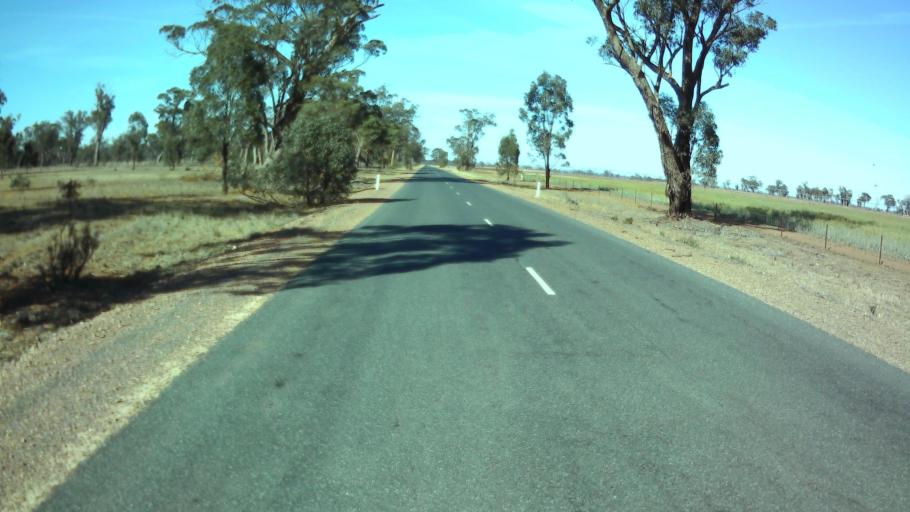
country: AU
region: New South Wales
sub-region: Weddin
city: Grenfell
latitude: -34.1158
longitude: 147.8193
